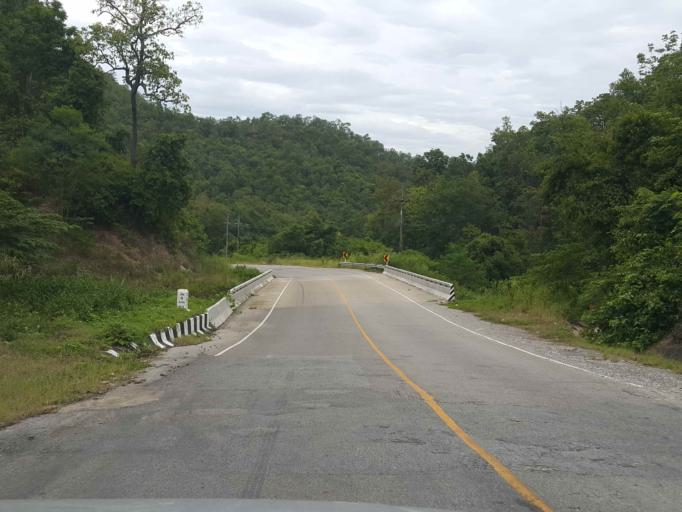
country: TH
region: Lampang
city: Thoen
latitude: 17.6409
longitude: 99.3055
